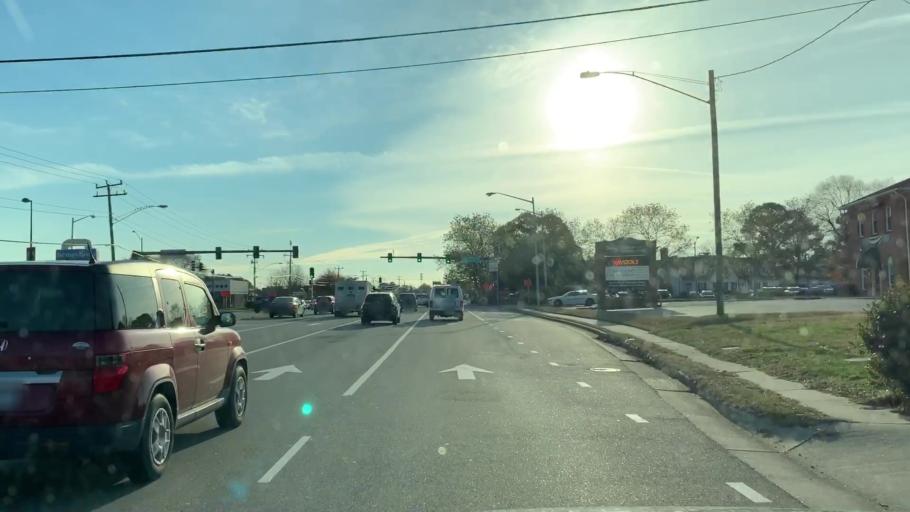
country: US
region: Virginia
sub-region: City of Chesapeake
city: Chesapeake
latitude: 36.8000
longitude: -76.1802
